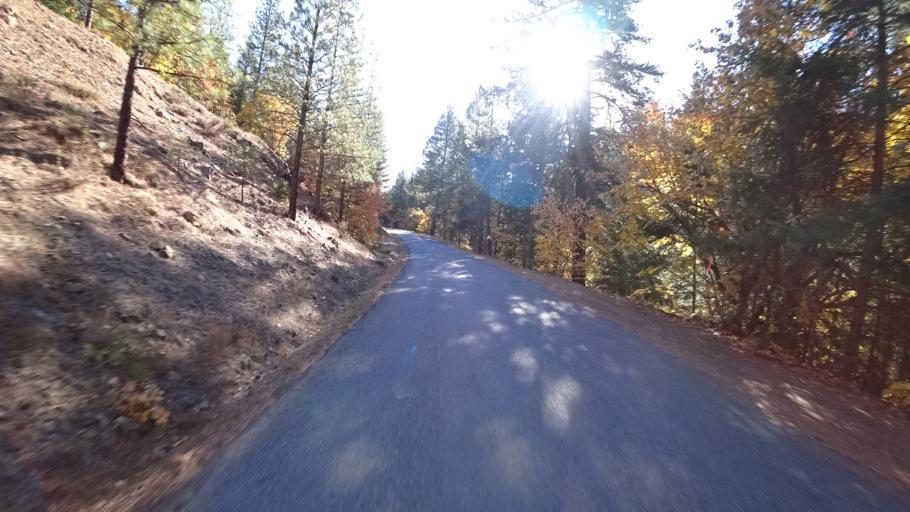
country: US
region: California
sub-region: Siskiyou County
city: Yreka
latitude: 41.6410
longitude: -123.0151
